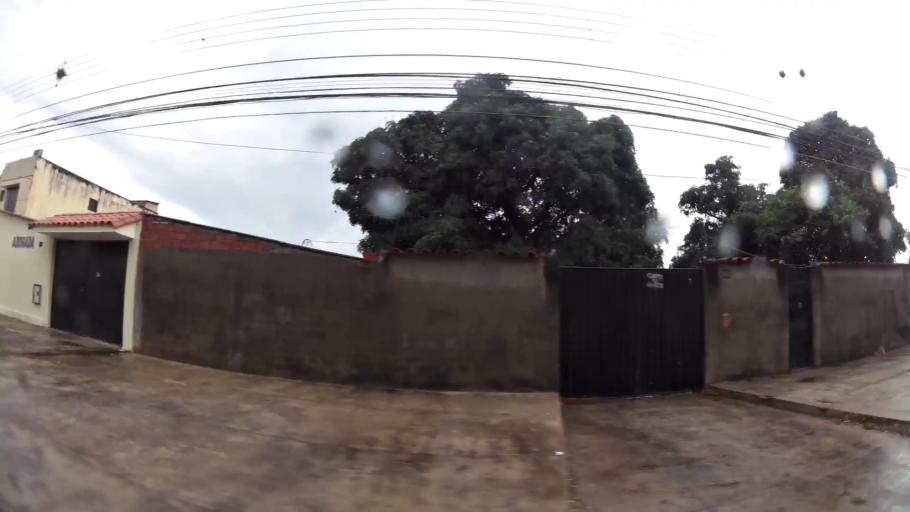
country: BO
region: Santa Cruz
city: Santa Cruz de la Sierra
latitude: -17.7646
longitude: -63.1520
